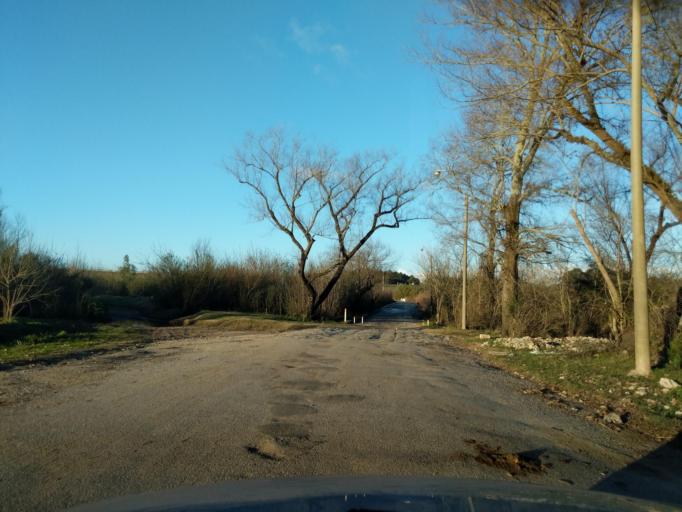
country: UY
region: Florida
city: Florida
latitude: -34.0920
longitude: -56.2067
